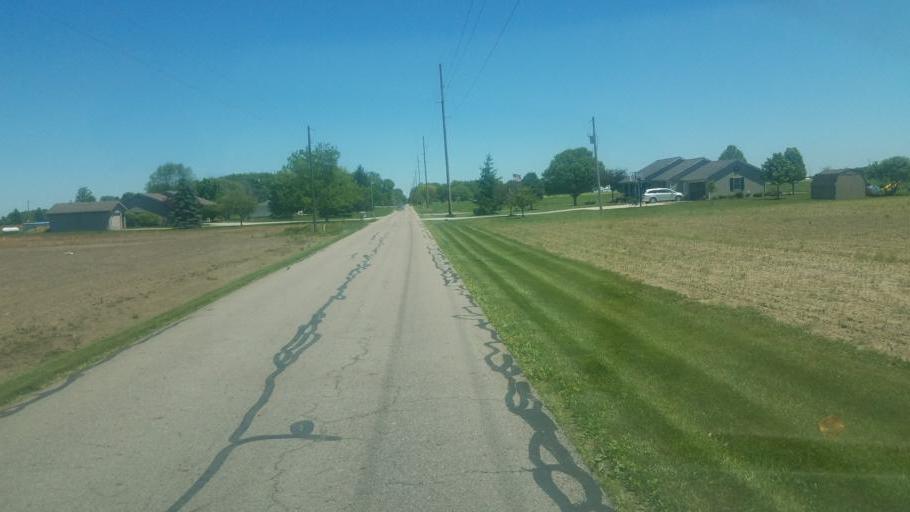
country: US
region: Ohio
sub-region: Darke County
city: Versailles
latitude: 40.2264
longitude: -84.4056
